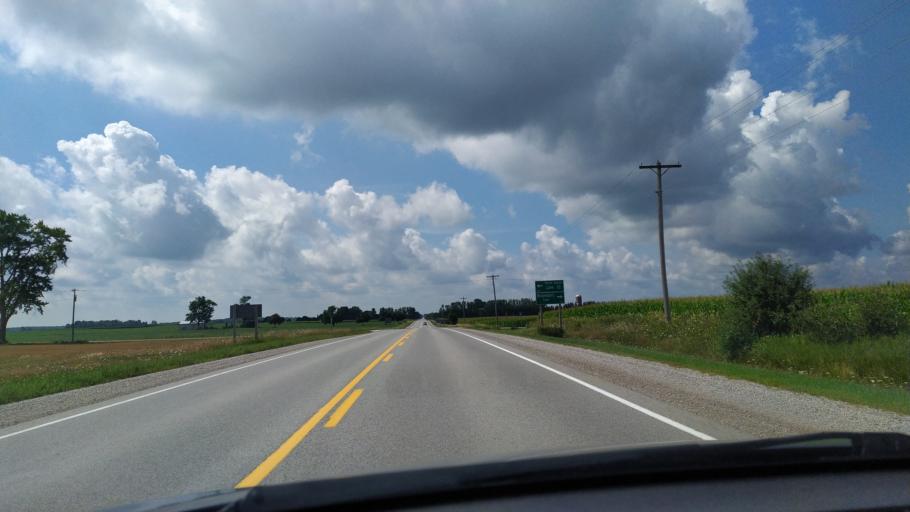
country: CA
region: Ontario
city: South Huron
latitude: 43.3569
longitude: -81.2861
